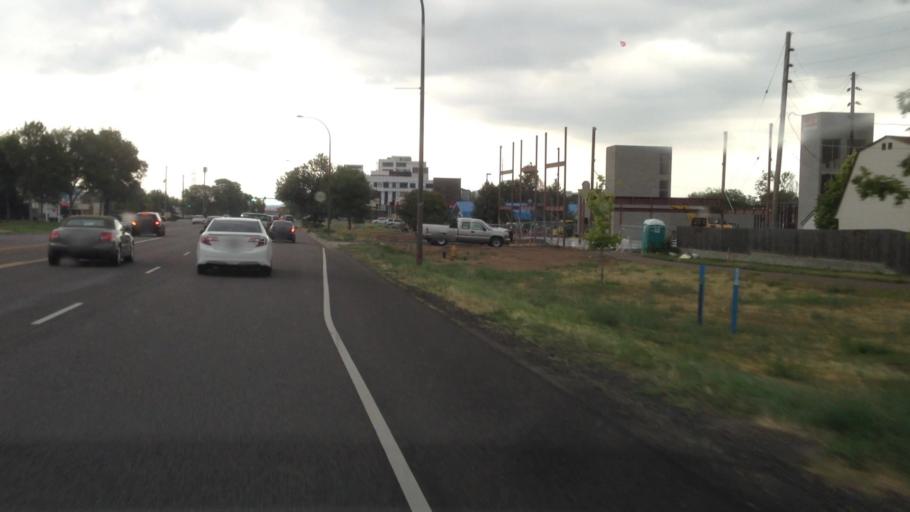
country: US
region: Colorado
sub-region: Jefferson County
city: Lakewood
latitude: 39.7110
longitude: -105.0660
